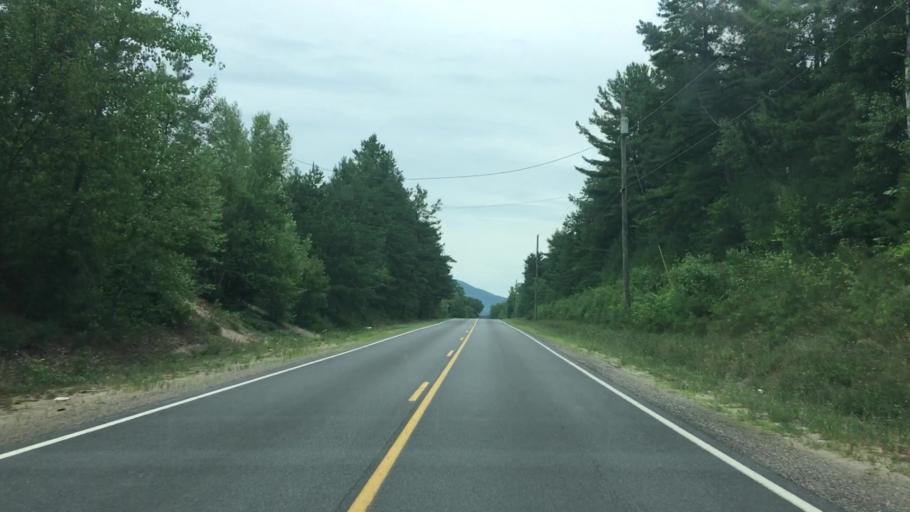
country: US
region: New York
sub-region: Essex County
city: Keeseville
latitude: 44.4710
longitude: -73.5930
